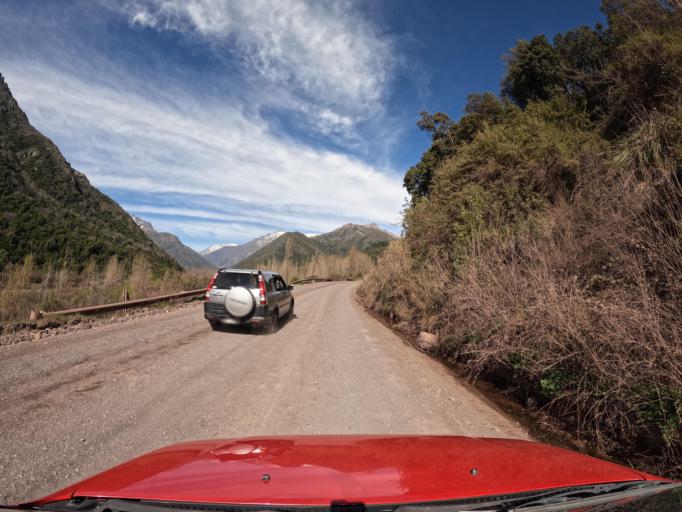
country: CL
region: O'Higgins
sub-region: Provincia de Colchagua
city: Chimbarongo
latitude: -35.0023
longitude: -70.7600
